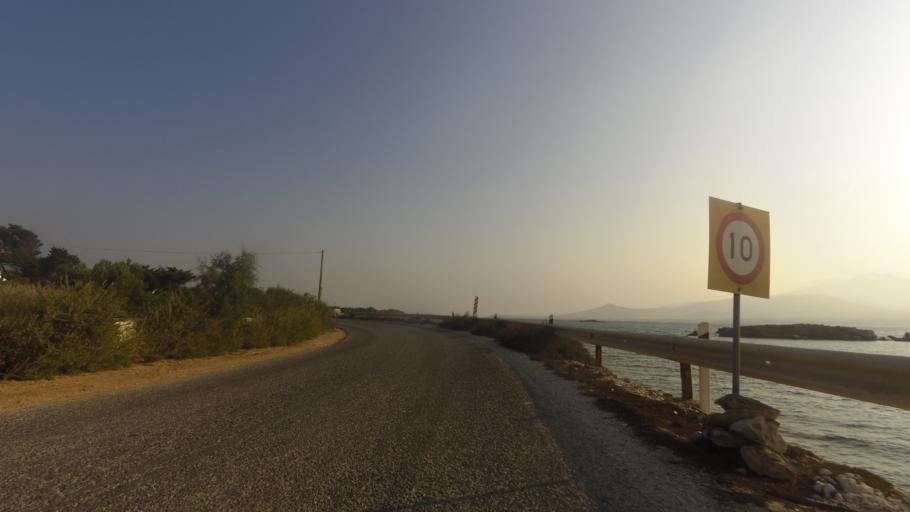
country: GR
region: South Aegean
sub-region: Nomos Kykladon
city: Antiparos
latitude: 37.0121
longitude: 25.0754
